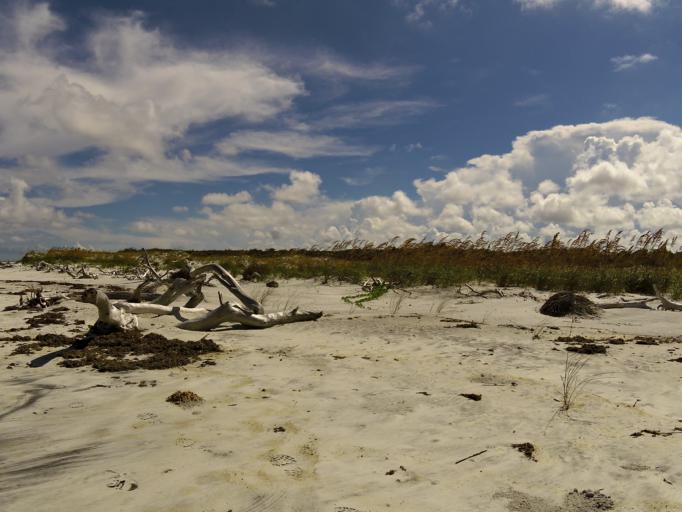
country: US
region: Florida
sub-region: Duval County
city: Atlantic Beach
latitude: 30.4847
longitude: -81.4157
